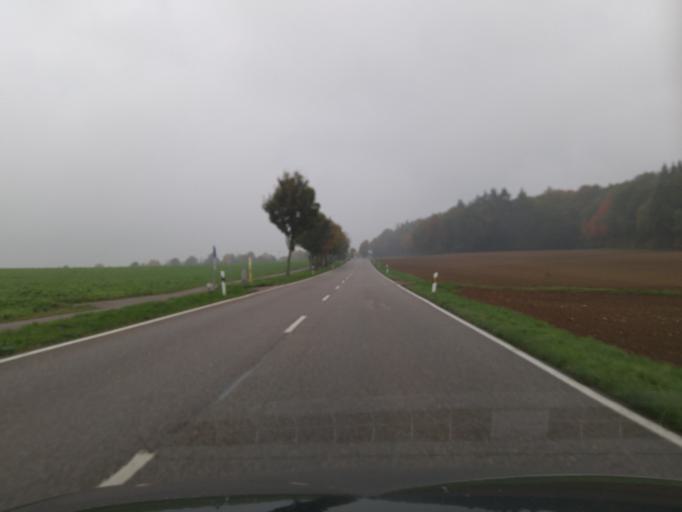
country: DE
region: Baden-Wuerttemberg
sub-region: Regierungsbezirk Stuttgart
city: Bad Rappenau
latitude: 49.2302
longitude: 9.1218
